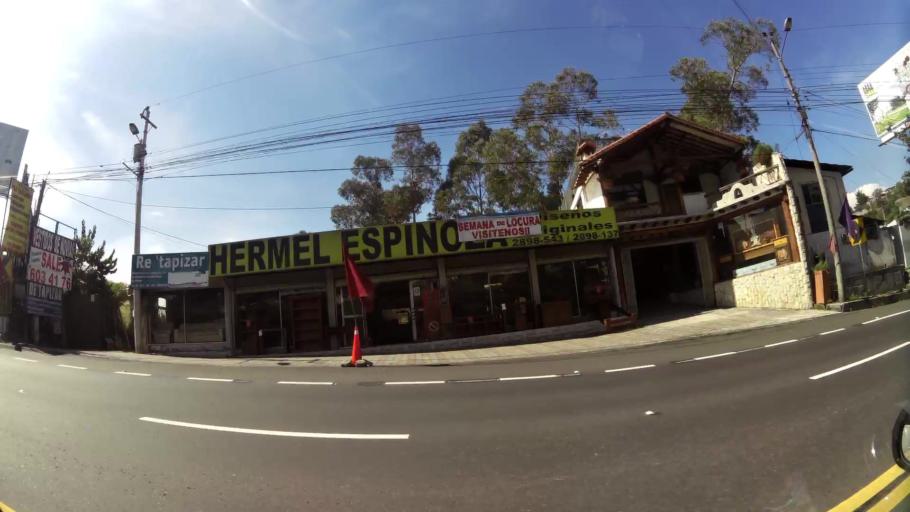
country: EC
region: Pichincha
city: Quito
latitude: -0.1935
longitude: -78.4433
